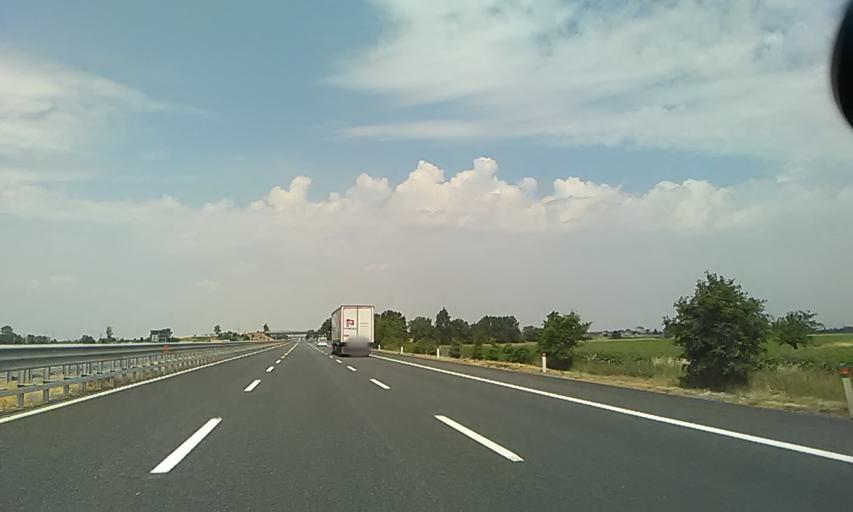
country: IT
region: Piedmont
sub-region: Provincia di Alessandria
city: Predosa
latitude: 44.7758
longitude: 8.6264
